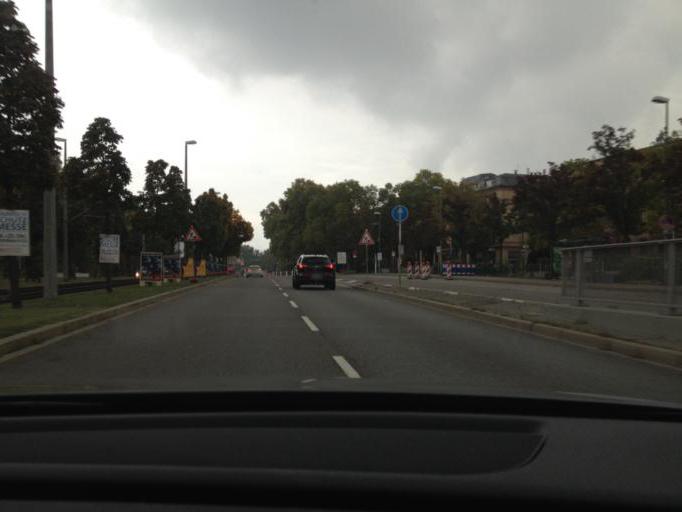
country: DE
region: Rheinland-Pfalz
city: Ludwigshafen am Rhein
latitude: 49.4934
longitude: 8.4352
